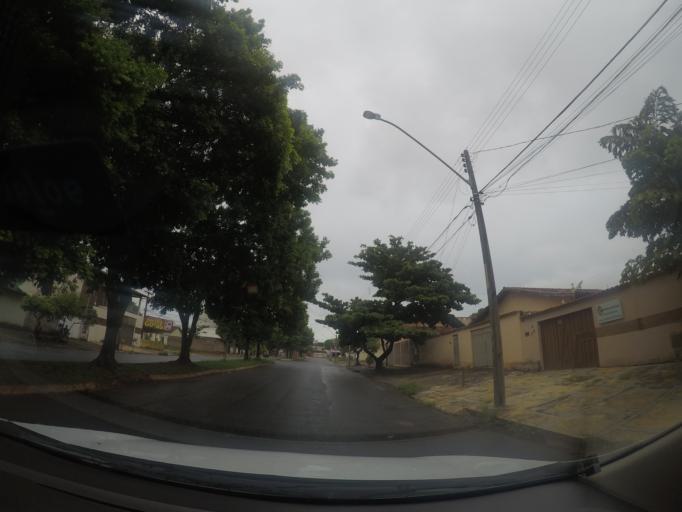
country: BR
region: Goias
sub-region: Goiania
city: Goiania
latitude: -16.7046
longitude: -49.3126
